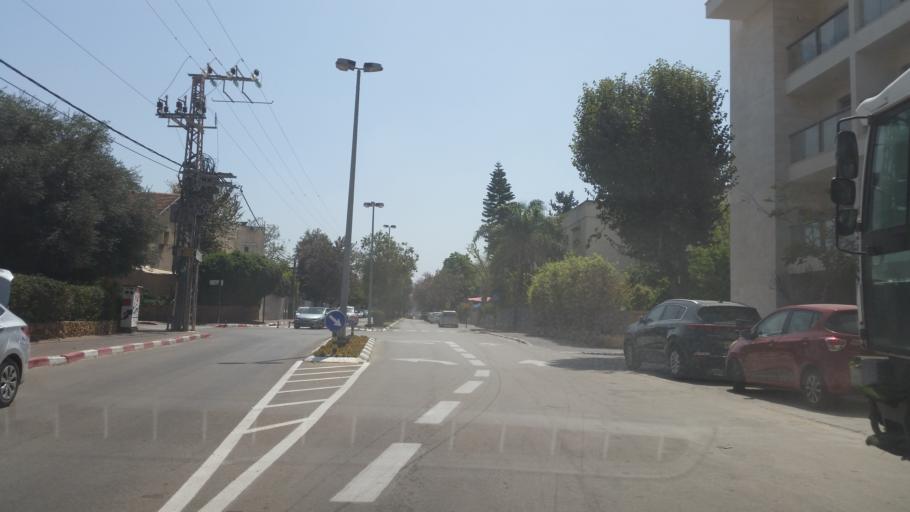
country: IL
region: Central District
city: Ra'anana
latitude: 32.1775
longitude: 34.8807
